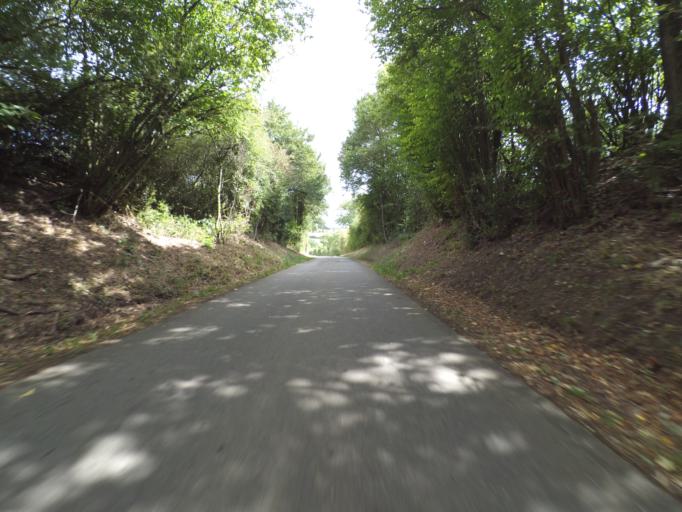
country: LU
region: Luxembourg
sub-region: Canton de Luxembourg
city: Weiler-la-Tour
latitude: 49.5462
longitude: 6.2181
